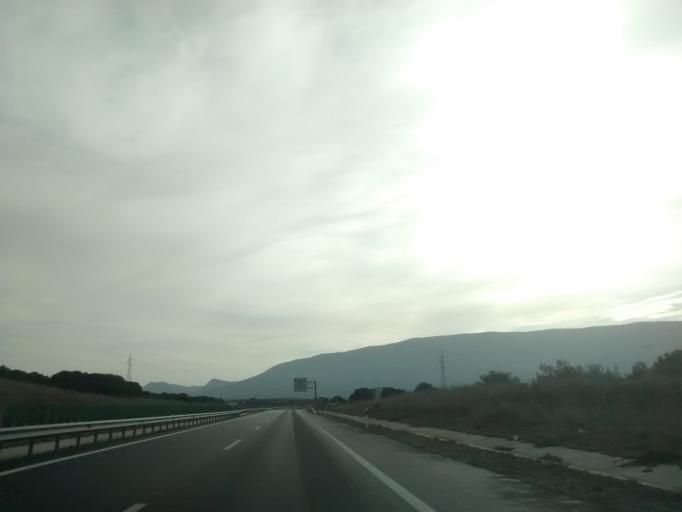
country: ES
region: Aragon
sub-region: Provincia de Zaragoza
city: Siguees
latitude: 42.6186
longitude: -1.0036
